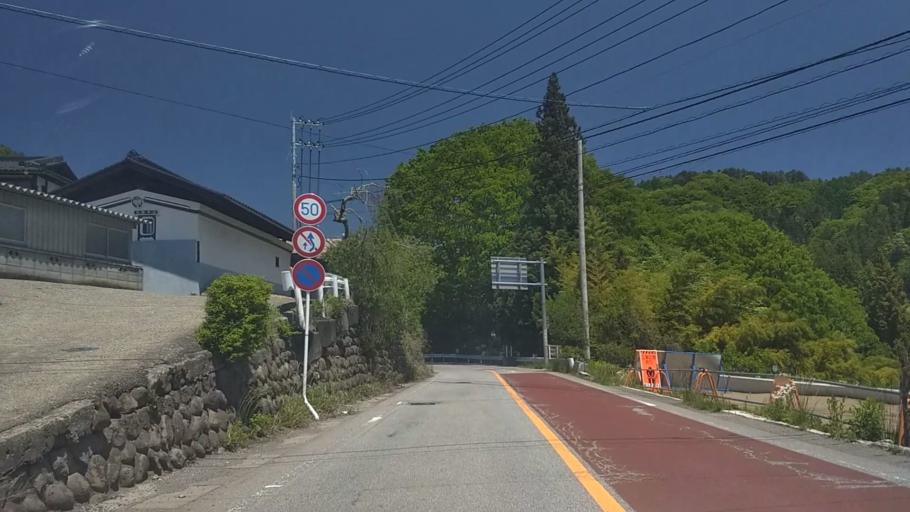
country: JP
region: Yamanashi
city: Nirasaki
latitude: 35.8738
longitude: 138.4290
